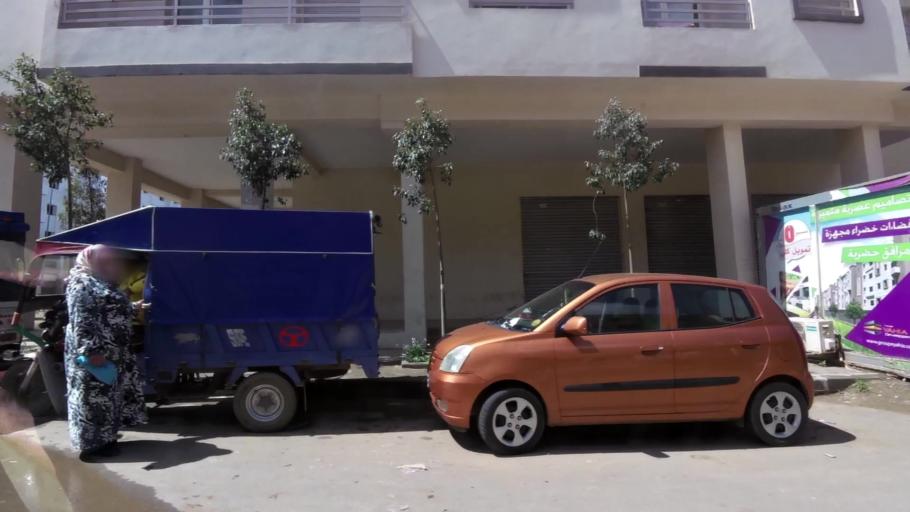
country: MA
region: Grand Casablanca
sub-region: Nouaceur
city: Dar Bouazza
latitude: 33.5331
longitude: -7.7308
